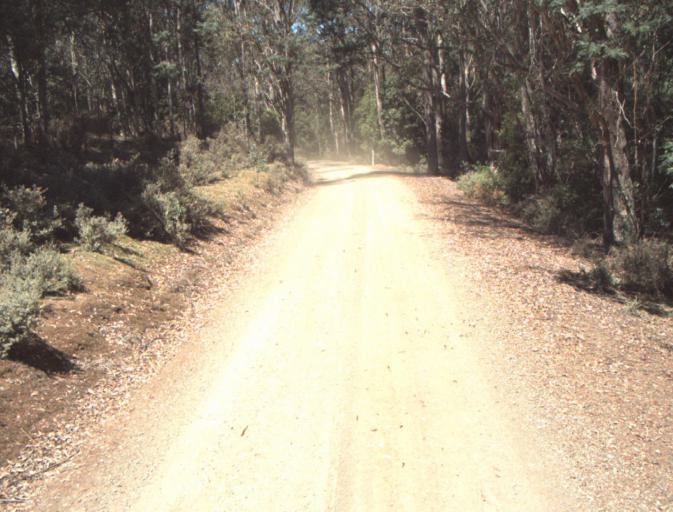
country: AU
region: Tasmania
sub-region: Dorset
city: Scottsdale
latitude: -41.3570
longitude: 147.4259
